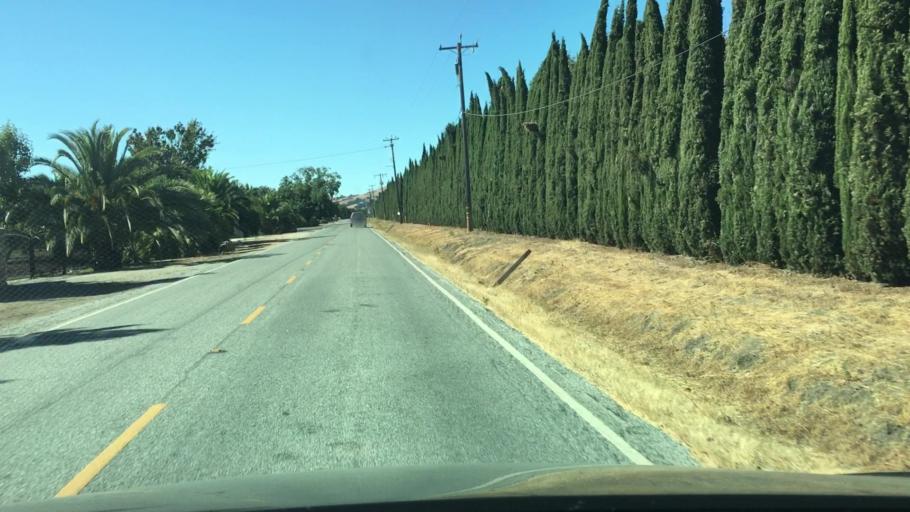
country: US
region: California
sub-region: Santa Clara County
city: San Martin
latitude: 37.1106
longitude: -121.5902
